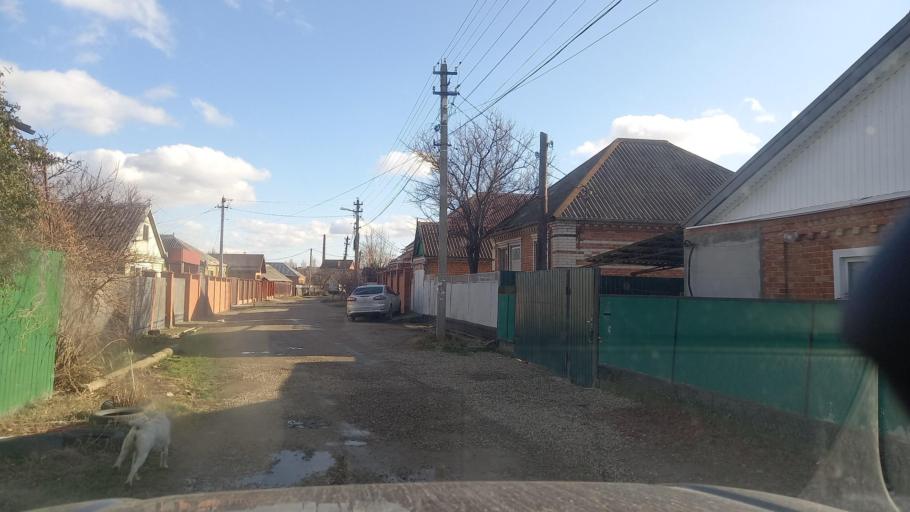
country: RU
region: Adygeya
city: Yablonovskiy
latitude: 44.9943
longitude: 38.9438
